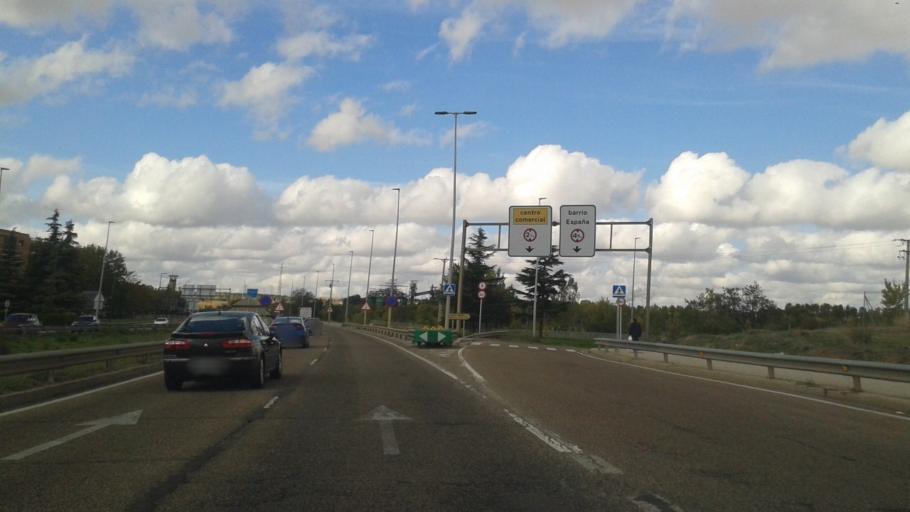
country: ES
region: Castille and Leon
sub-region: Provincia de Valladolid
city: Valladolid
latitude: 41.6704
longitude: -4.7076
